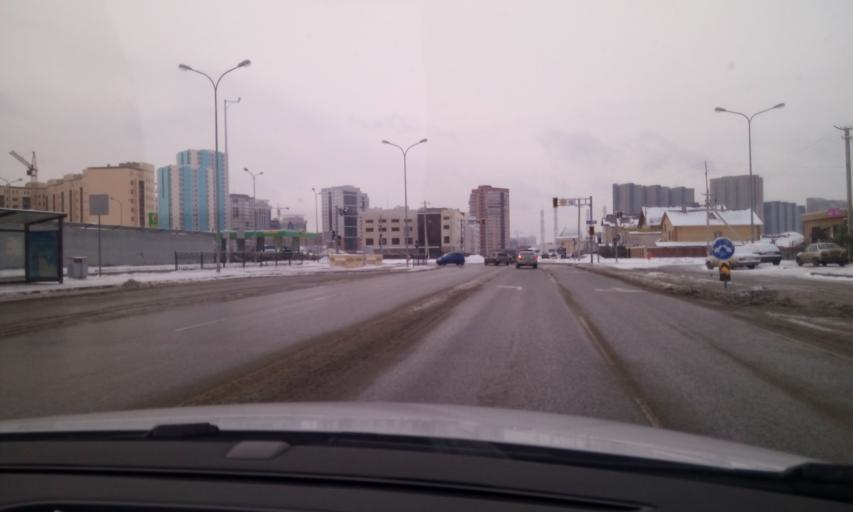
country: KZ
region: Astana Qalasy
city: Astana
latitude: 51.1288
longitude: 71.4863
